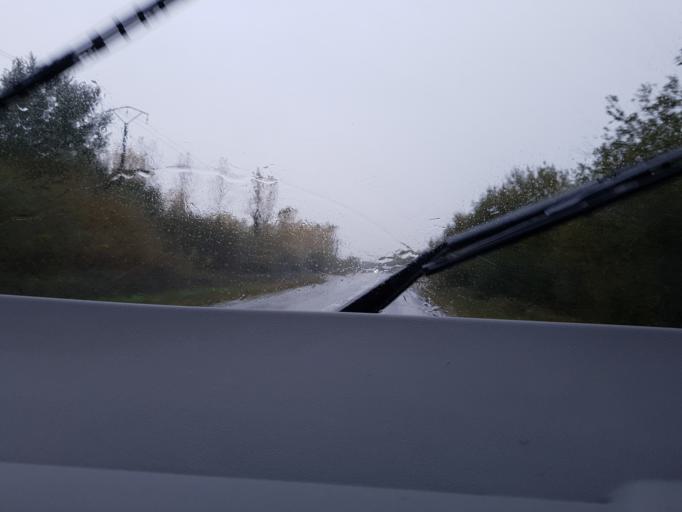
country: FR
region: Aquitaine
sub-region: Departement de la Gironde
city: Saint-Louis-de-Montferrand
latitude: 44.9501
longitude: -0.5193
